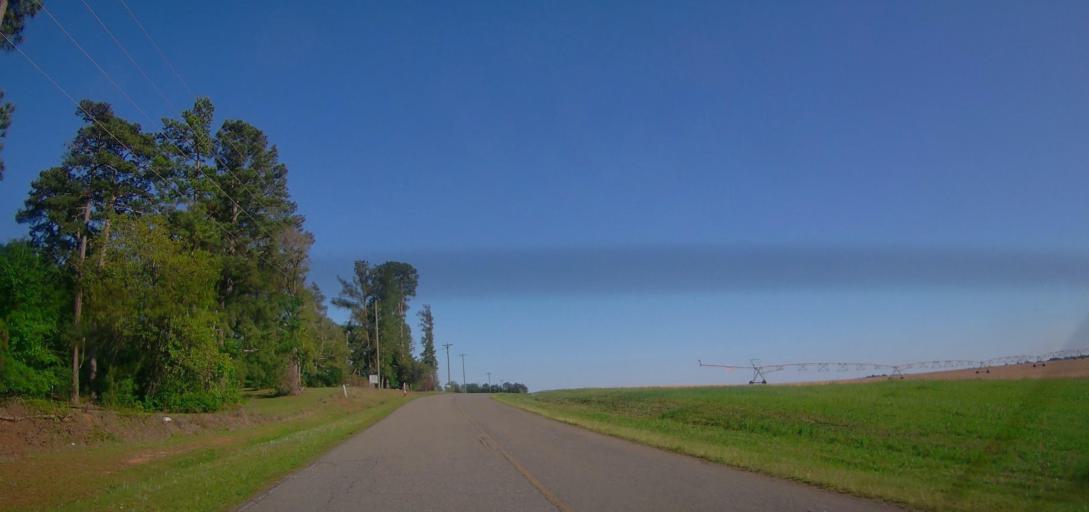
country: US
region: Georgia
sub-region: Houston County
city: Perry
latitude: 32.4382
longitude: -83.7873
